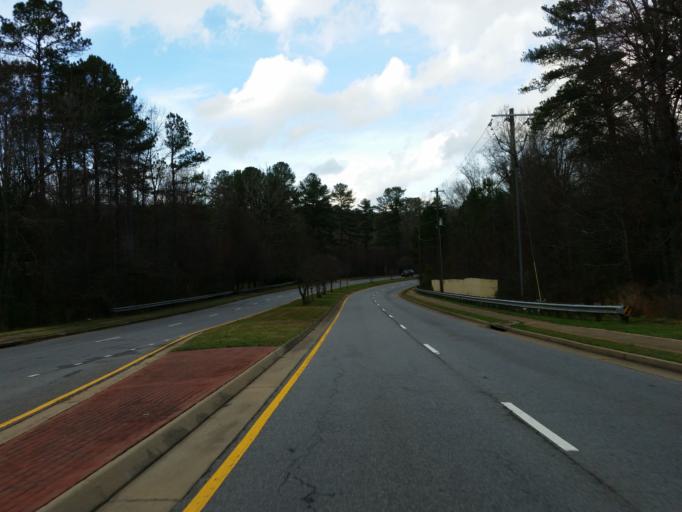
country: US
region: Georgia
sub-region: Cobb County
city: Marietta
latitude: 33.9904
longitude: -84.4890
